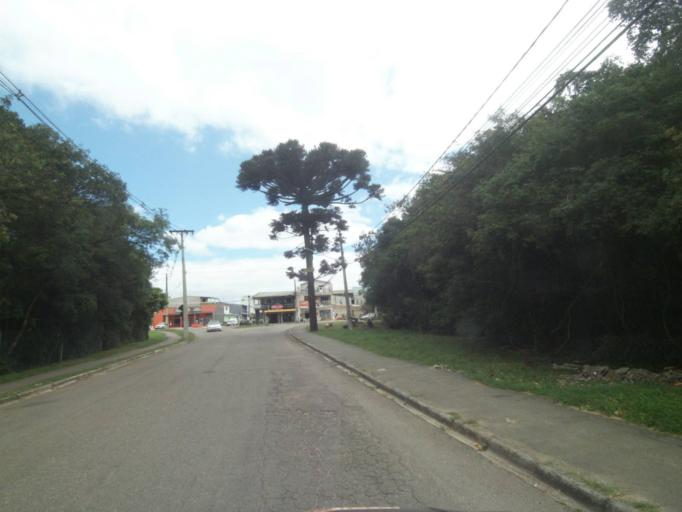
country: BR
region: Parana
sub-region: Sao Jose Dos Pinhais
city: Sao Jose dos Pinhais
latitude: -25.5545
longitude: -49.2622
